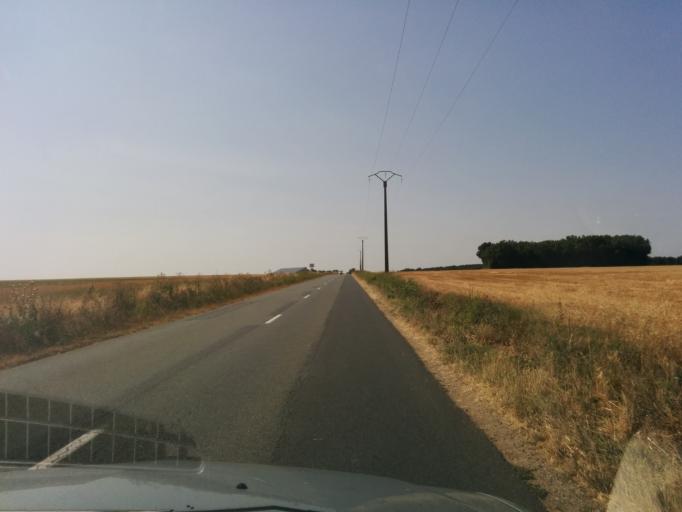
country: FR
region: Poitou-Charentes
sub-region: Departement de la Vienne
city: Mirebeau
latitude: 46.7354
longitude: 0.1896
